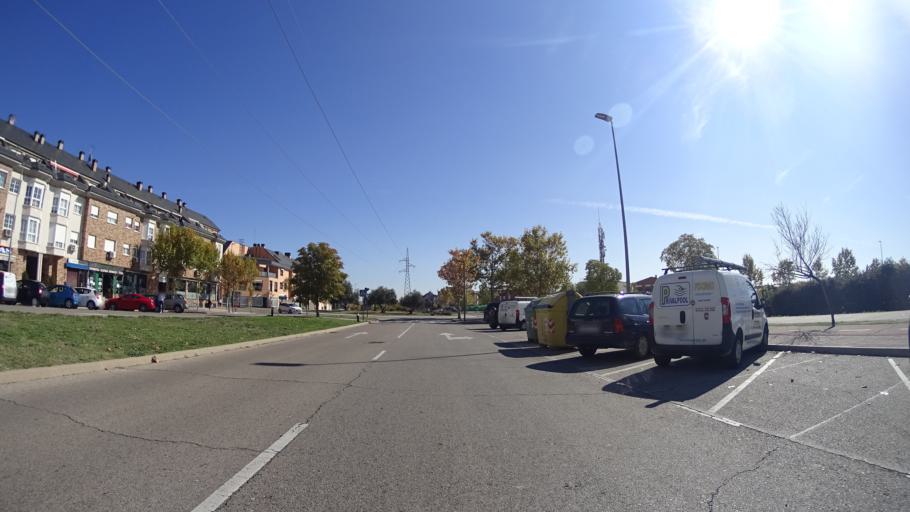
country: ES
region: Madrid
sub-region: Provincia de Madrid
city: Villanueva del Pardillo
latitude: 40.4947
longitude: -3.9628
